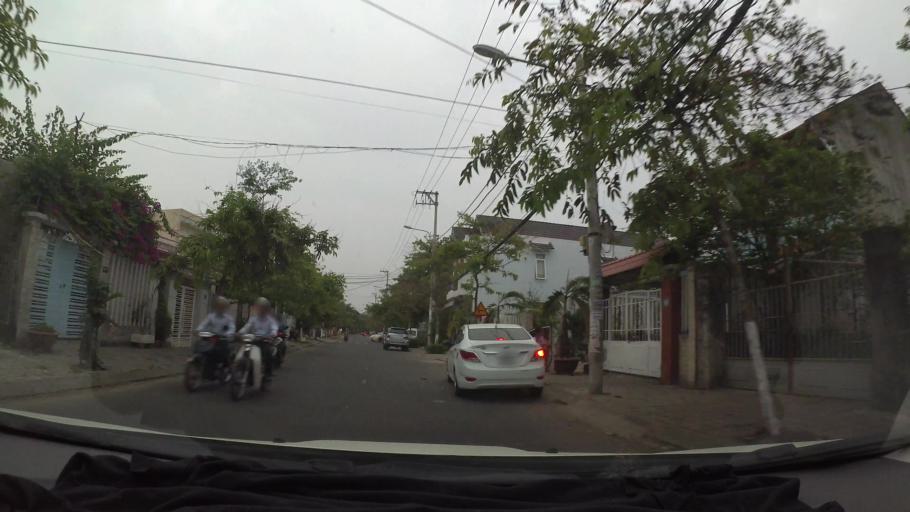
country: VN
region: Da Nang
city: Thanh Khe
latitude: 16.0513
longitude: 108.1758
